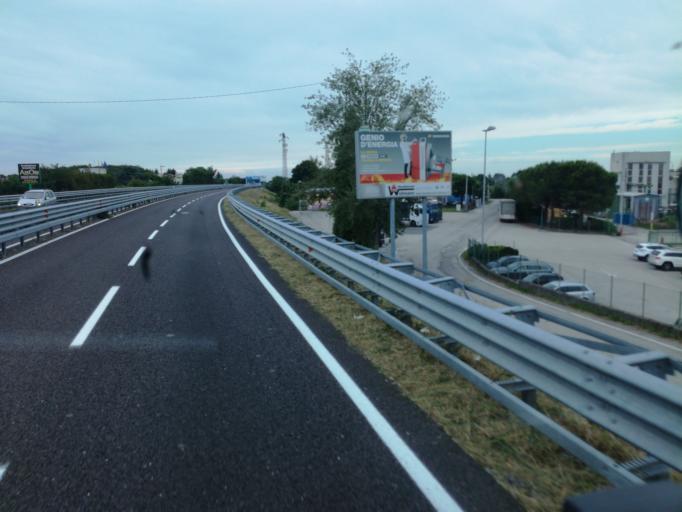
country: IT
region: Veneto
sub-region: Provincia di Vicenza
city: Pove del Grappa
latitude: 45.7879
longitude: 11.7468
